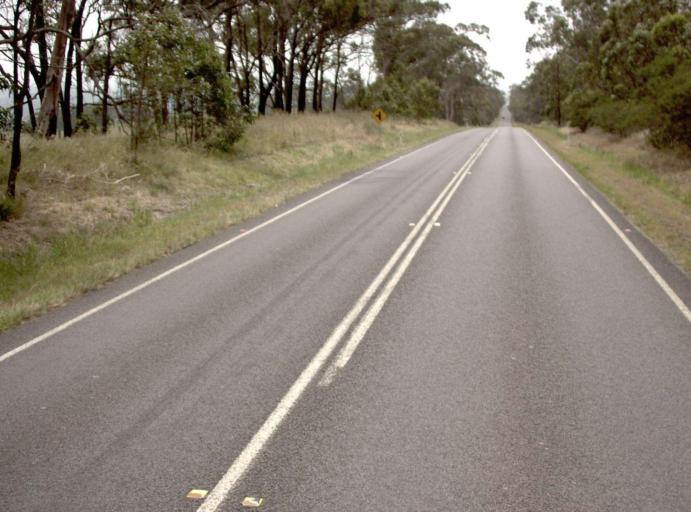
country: AU
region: Victoria
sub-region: Latrobe
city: Traralgon
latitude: -38.5169
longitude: 146.7077
